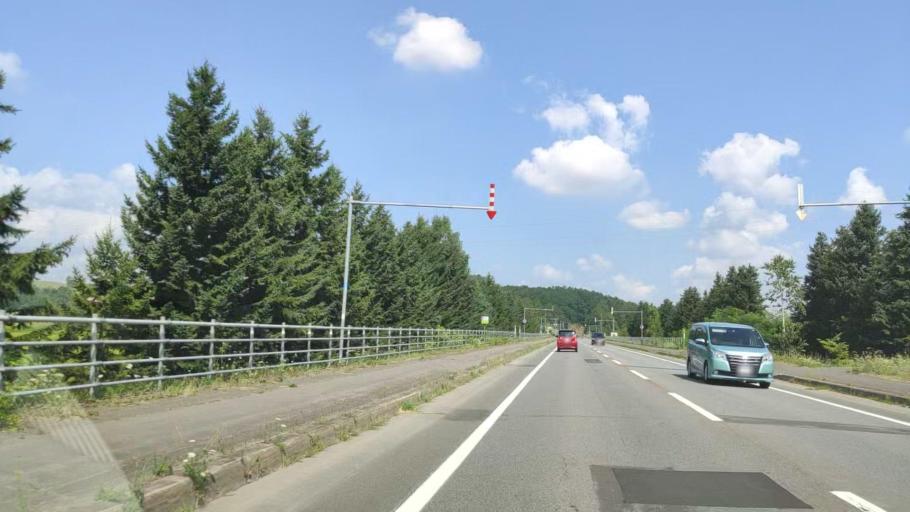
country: JP
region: Hokkaido
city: Shimo-furano
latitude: 43.4663
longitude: 142.4554
